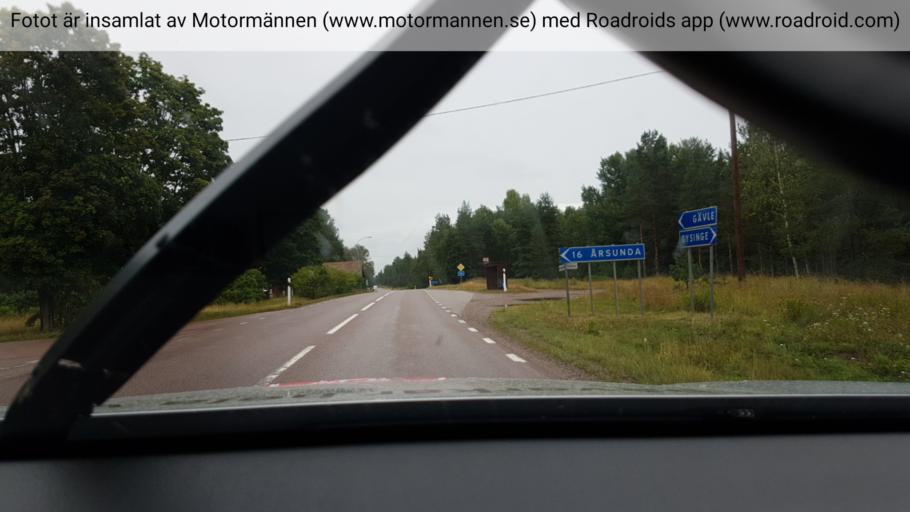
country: SE
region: Gaevleborg
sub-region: Gavle Kommun
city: Hedesunda
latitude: 60.4988
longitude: 16.9394
